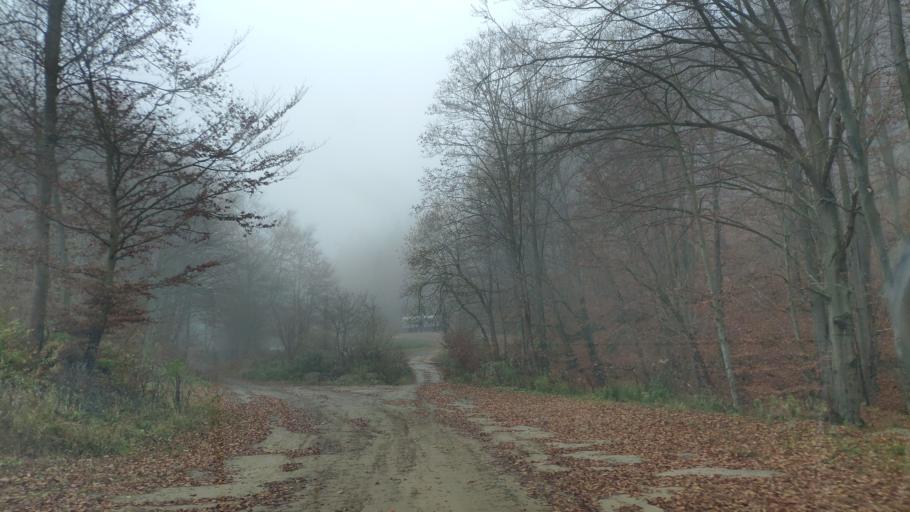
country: SK
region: Presovsky
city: Sabinov
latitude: 49.1571
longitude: 21.2019
